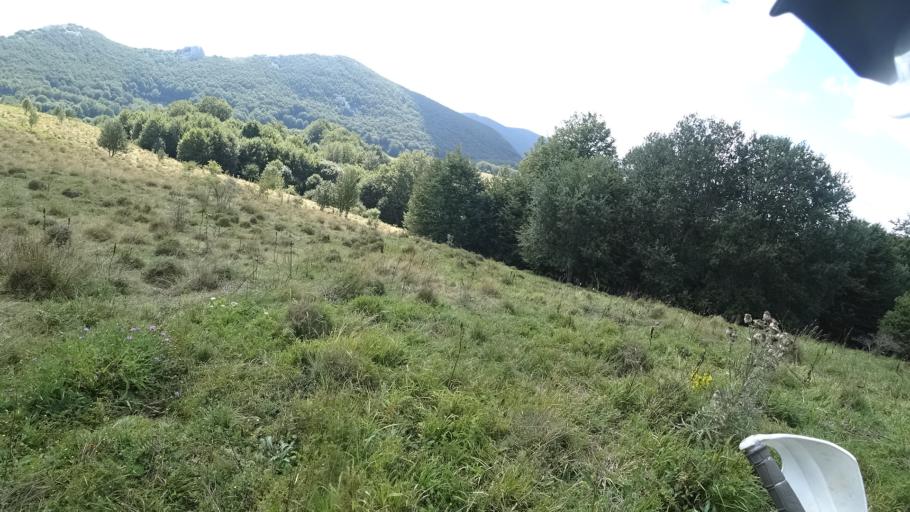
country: HR
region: Zadarska
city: Gracac
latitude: 44.4225
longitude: 15.9968
